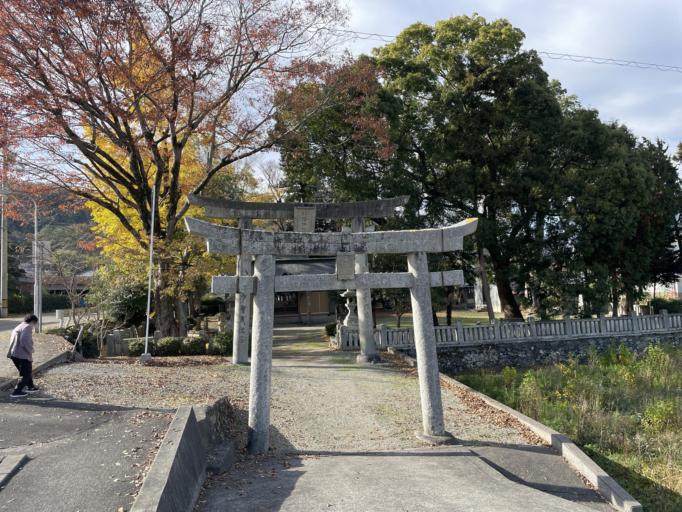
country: JP
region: Tokushima
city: Wakimachi
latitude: 34.0508
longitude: 134.1726
